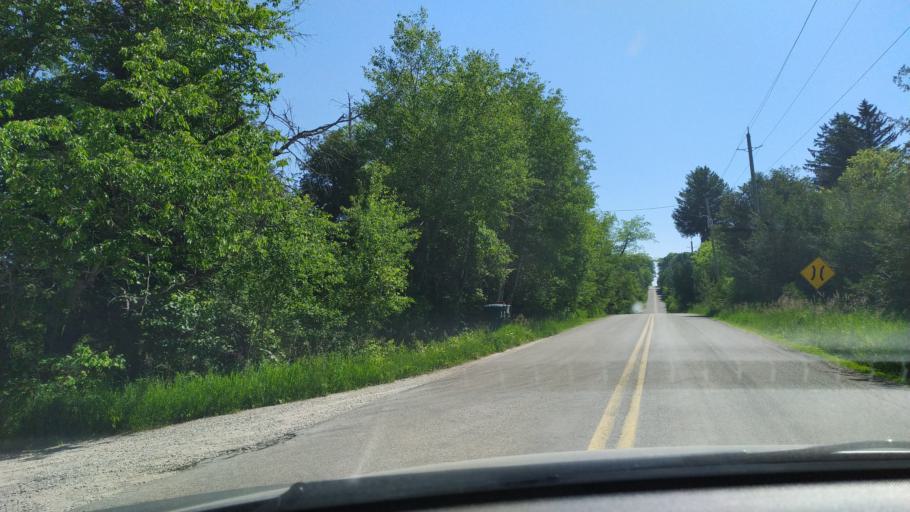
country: CA
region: Ontario
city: Waterloo
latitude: 43.4716
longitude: -80.6336
